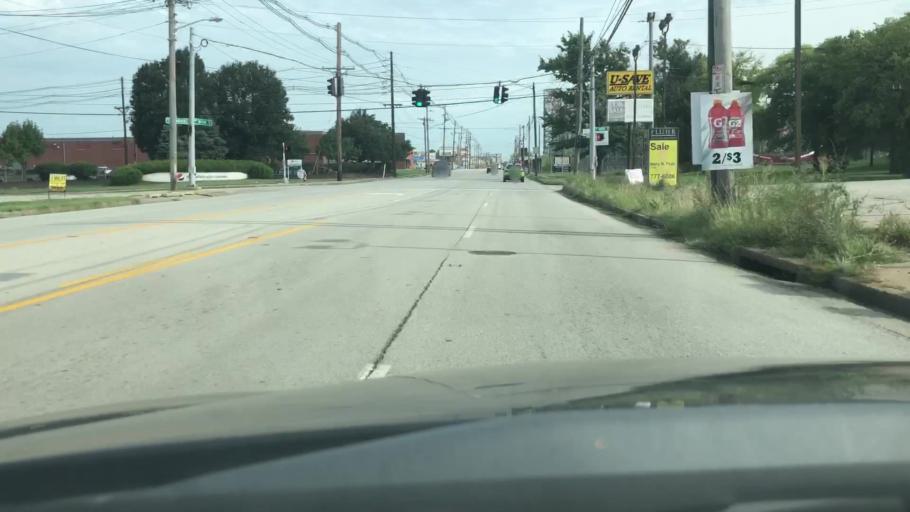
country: US
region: Kentucky
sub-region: Jefferson County
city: Audubon Park
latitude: 38.1936
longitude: -85.7509
